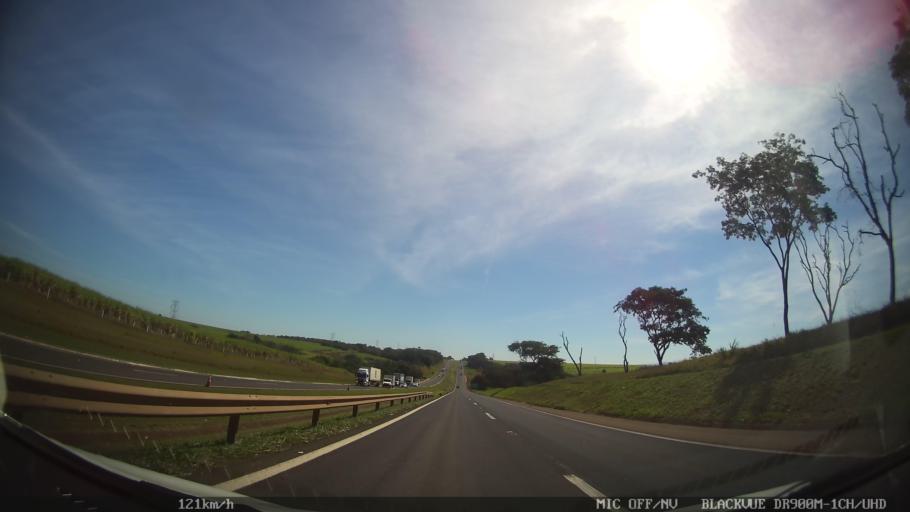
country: BR
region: Sao Paulo
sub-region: Porto Ferreira
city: Porto Ferreira
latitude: -21.9192
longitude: -47.4728
